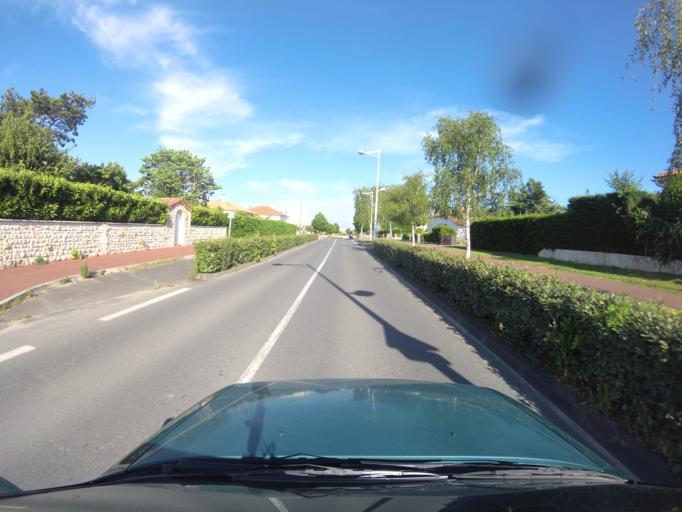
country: FR
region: Poitou-Charentes
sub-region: Departement de la Charente-Maritime
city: Royan
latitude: 45.6353
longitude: -1.0253
